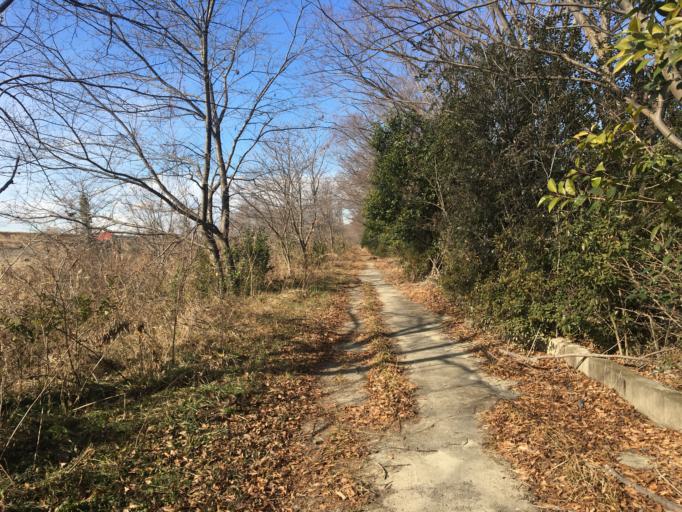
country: JP
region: Saitama
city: Shiki
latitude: 35.8535
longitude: 139.5962
